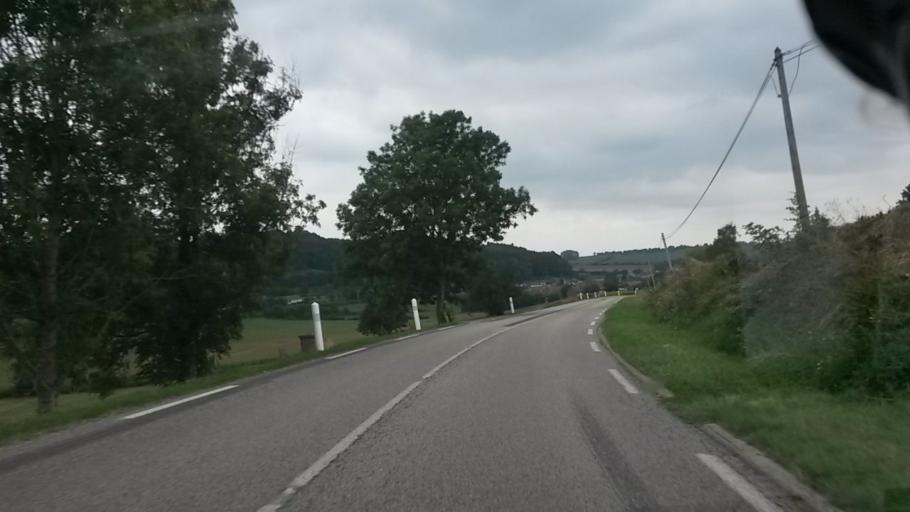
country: FR
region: Haute-Normandie
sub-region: Departement de la Seine-Maritime
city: Gaillefontaine
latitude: 49.6606
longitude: 1.6278
